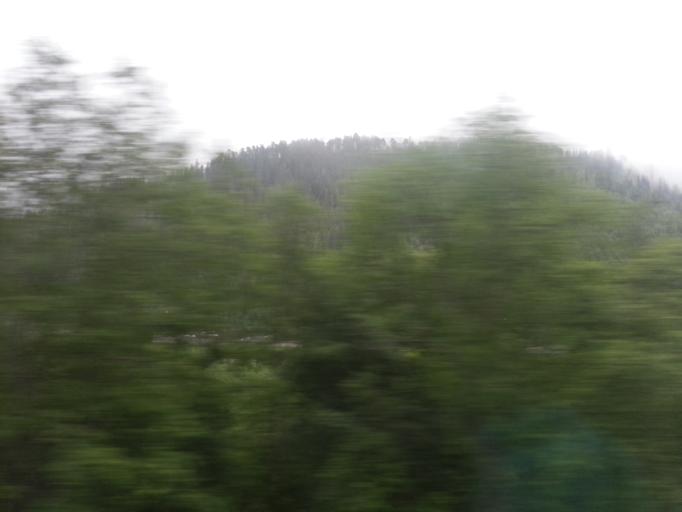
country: NO
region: Sor-Trondelag
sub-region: Midtre Gauldal
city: Storen
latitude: 63.0278
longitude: 10.2549
